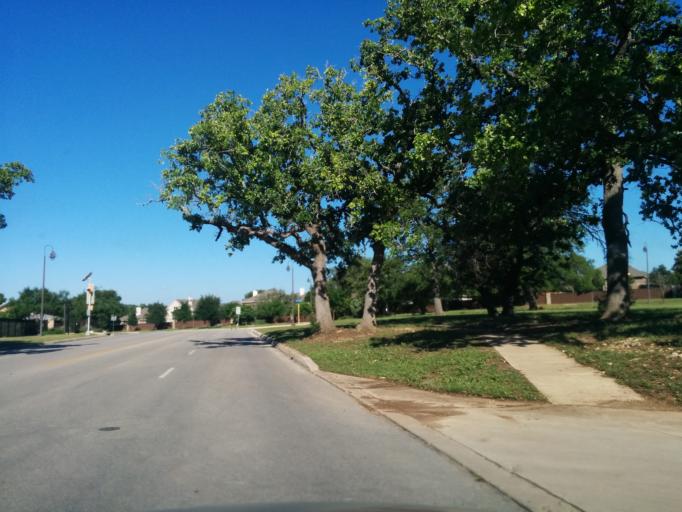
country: US
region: Texas
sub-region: Bexar County
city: Cross Mountain
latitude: 29.6720
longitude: -98.6478
